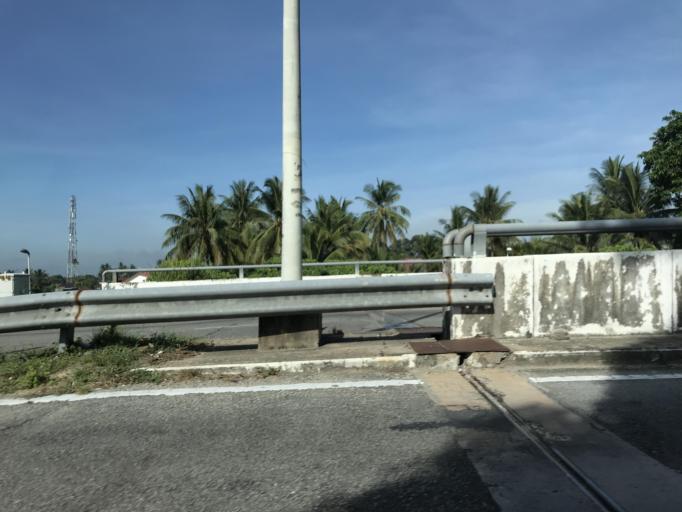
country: MY
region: Kelantan
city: Kampong Kadok
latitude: 6.0533
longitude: 102.2161
